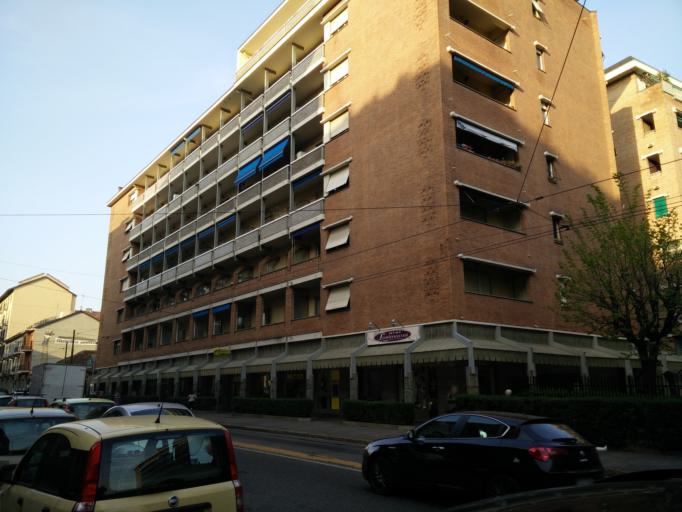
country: IT
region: Piedmont
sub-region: Provincia di Torino
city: Moncalieri
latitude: 45.0280
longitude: 7.6677
